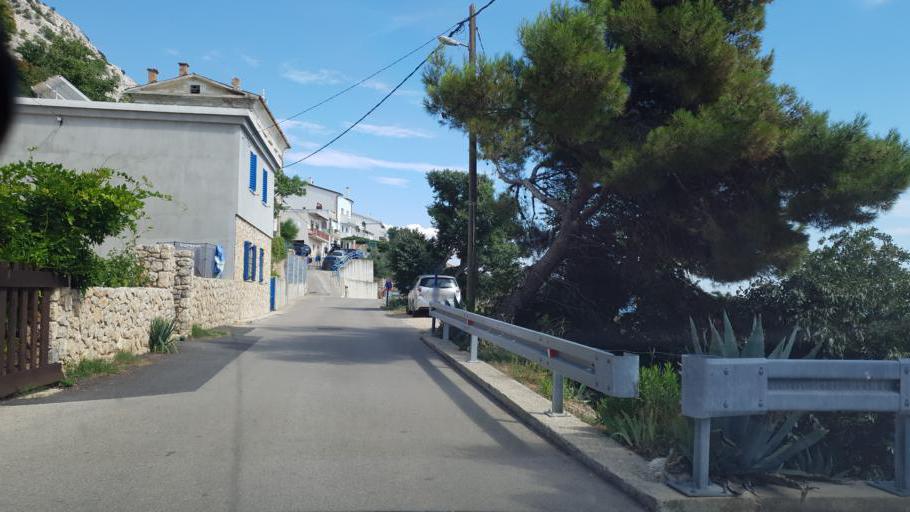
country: HR
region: Primorsko-Goranska
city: Punat
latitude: 44.9598
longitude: 14.6868
